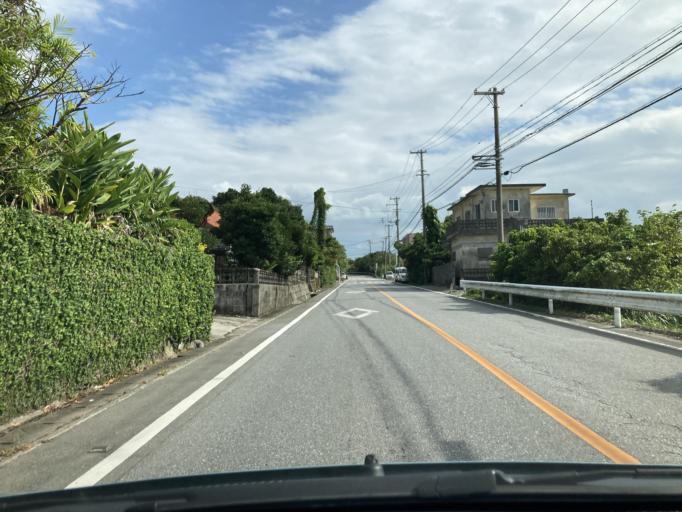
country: JP
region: Okinawa
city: Ginowan
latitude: 26.2706
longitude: 127.7815
